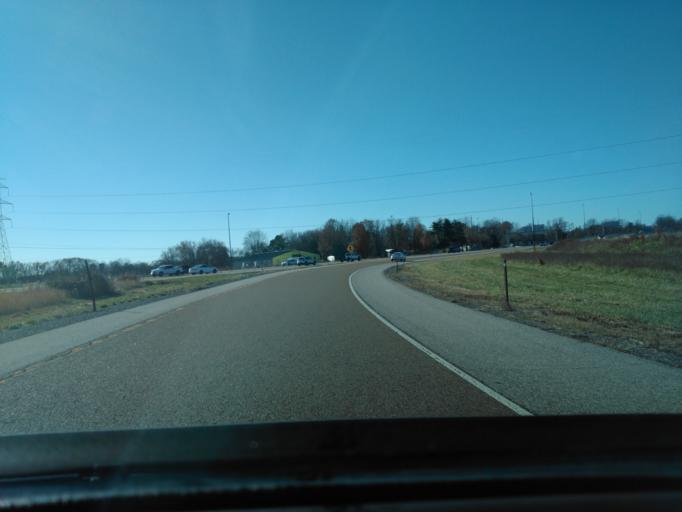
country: US
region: Illinois
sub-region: Madison County
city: Maryville
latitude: 38.7171
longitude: -89.9218
